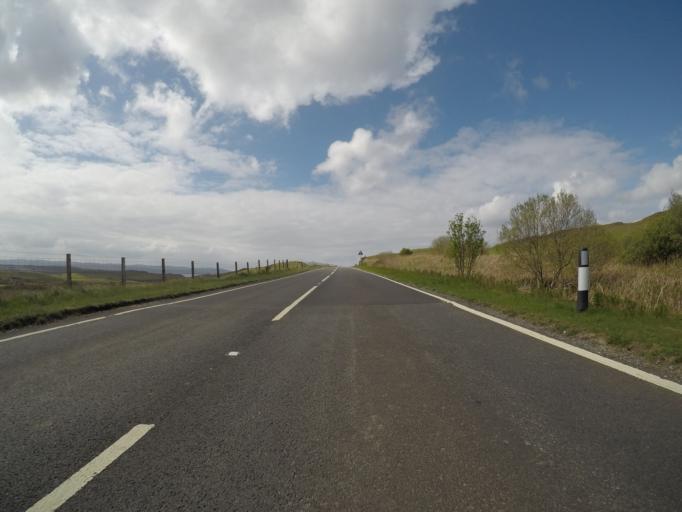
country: GB
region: Scotland
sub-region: Highland
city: Portree
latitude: 57.5318
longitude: -6.3526
